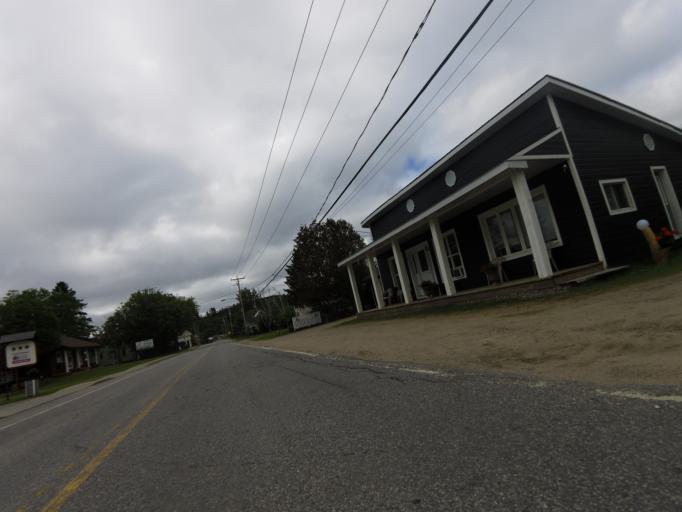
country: CA
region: Quebec
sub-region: Outaouais
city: Shawville
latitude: 45.8518
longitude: -76.4304
